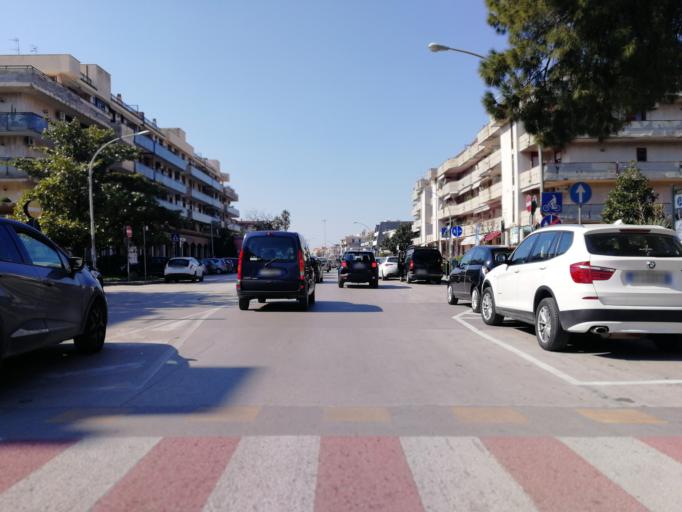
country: IT
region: Campania
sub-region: Provincia di Caserta
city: Santa Maria Capua Vetere
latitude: 41.0901
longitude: 14.2553
